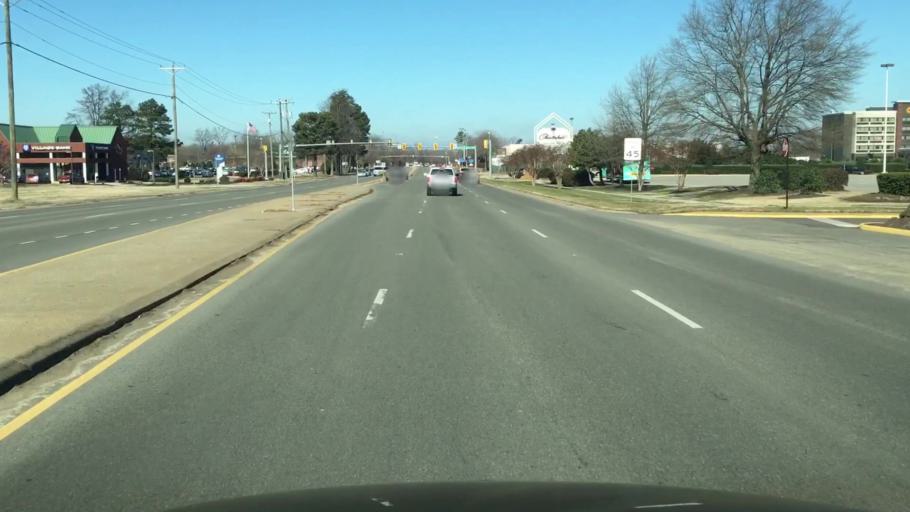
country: US
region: Virginia
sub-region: Chesterfield County
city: Bon Air
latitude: 37.5067
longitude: -77.6122
